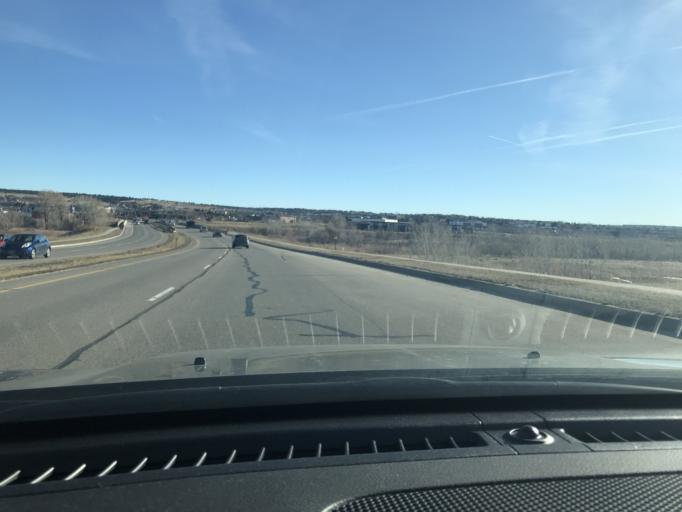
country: US
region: Colorado
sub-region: Douglas County
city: Stonegate
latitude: 39.5341
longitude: -104.7849
